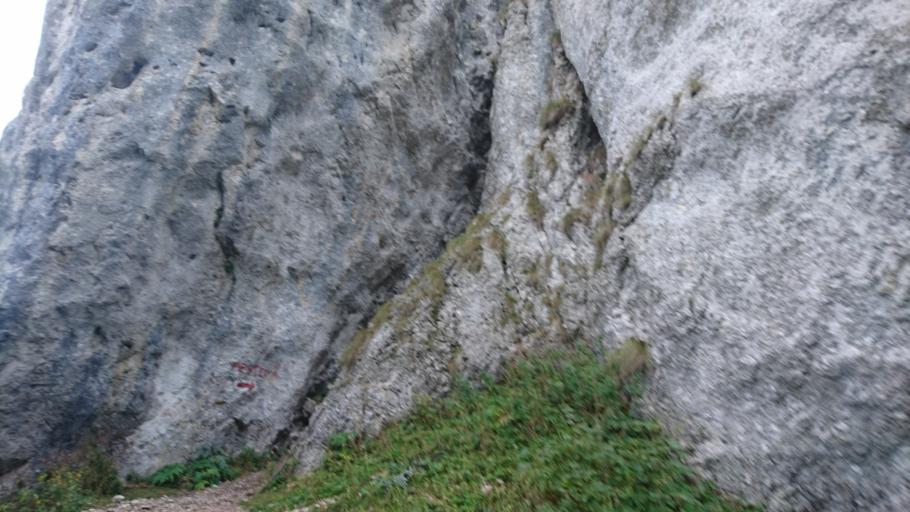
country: RO
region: Brasov
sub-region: Municipiul Sacele
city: Sacele
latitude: 45.5685
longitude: 25.6654
